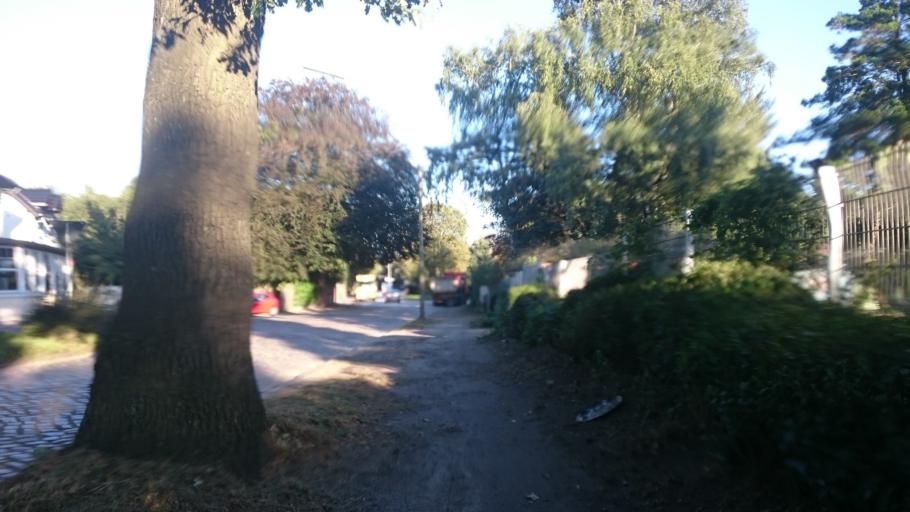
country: DE
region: Hamburg
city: Stellingen
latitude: 53.5714
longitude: 9.9149
